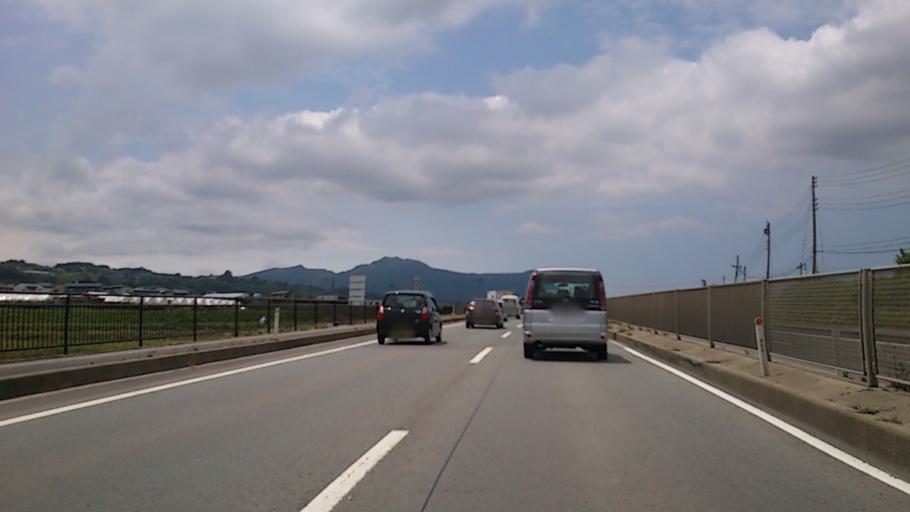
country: JP
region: Yamagata
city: Kaminoyama
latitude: 38.1975
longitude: 140.3144
